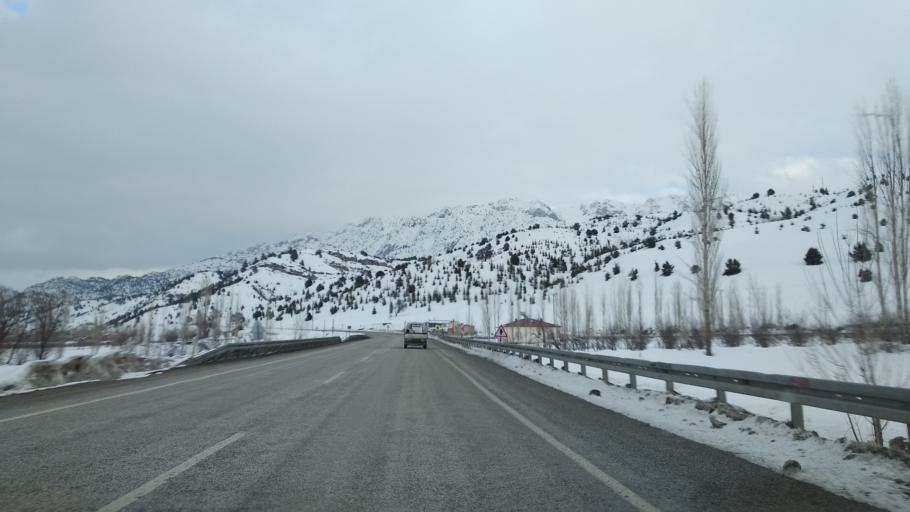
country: TR
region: Kahramanmaras
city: Goksun
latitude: 37.9974
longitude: 36.5286
